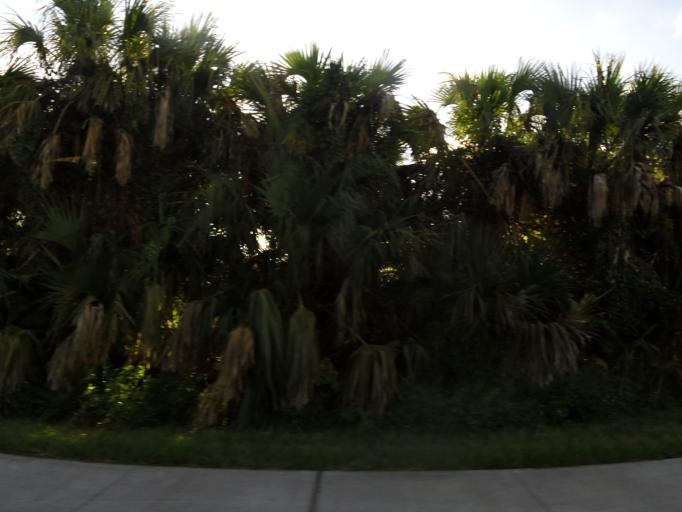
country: US
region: Florida
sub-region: Saint Johns County
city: Sawgrass
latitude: 30.1946
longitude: -81.3670
